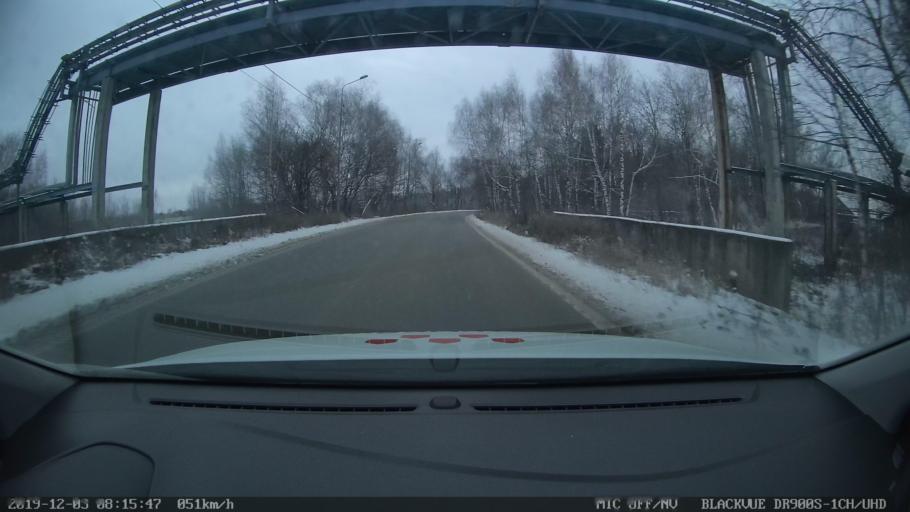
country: RU
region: Tatarstan
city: Staroye Arakchino
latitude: 55.8846
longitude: 48.9688
